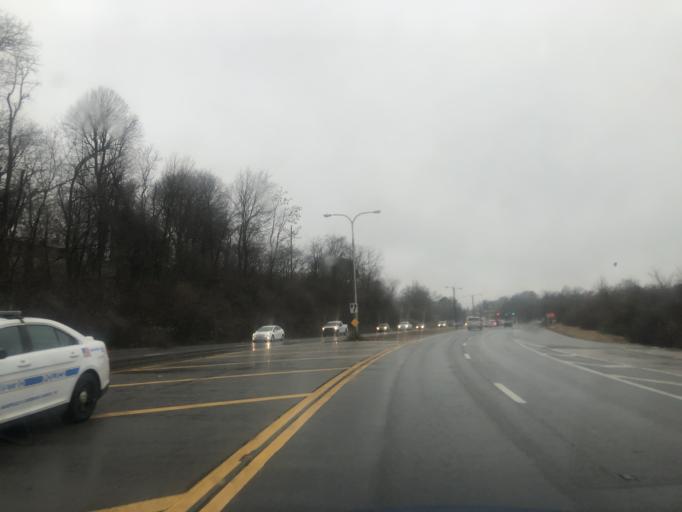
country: US
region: Tennessee
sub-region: Davidson County
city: Oak Hill
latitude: 36.1089
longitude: -86.7245
